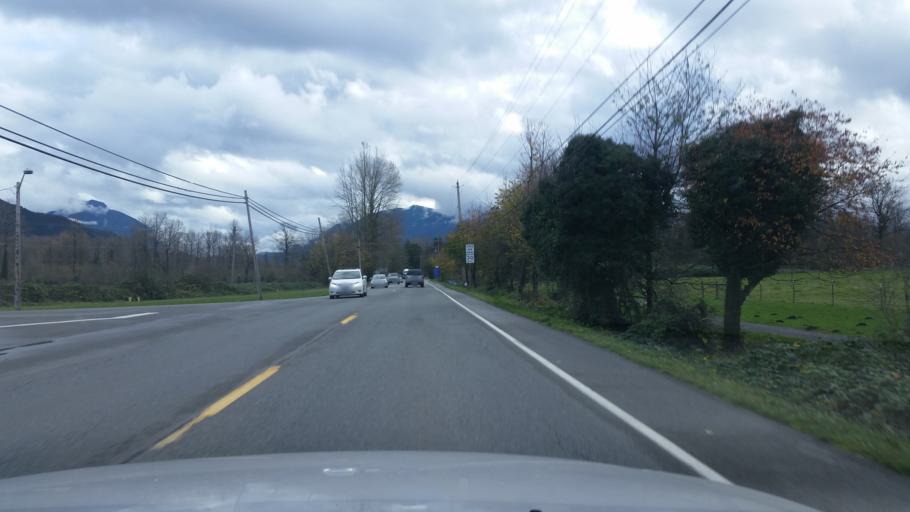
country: US
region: Washington
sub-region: King County
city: North Bend
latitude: 47.5030
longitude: -121.7941
